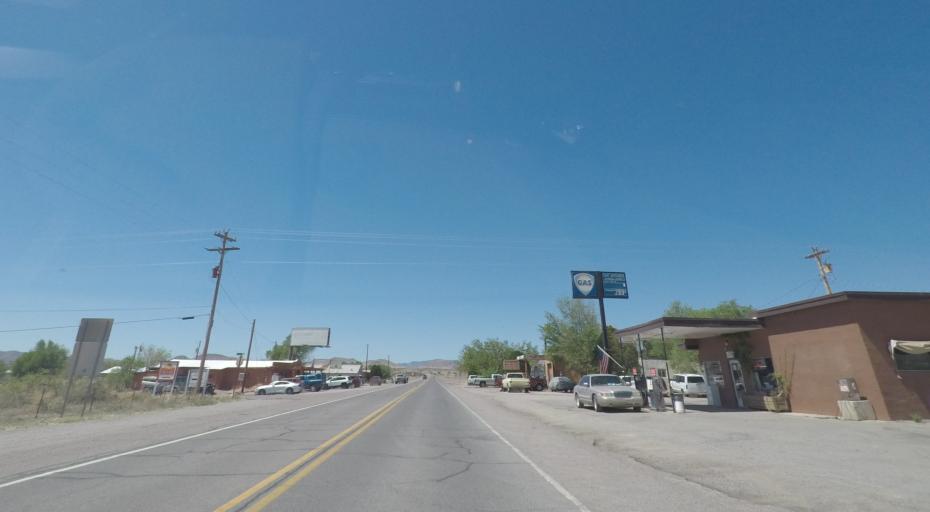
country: US
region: New Mexico
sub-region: Socorro County
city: Socorro
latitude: 33.9178
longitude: -106.8683
